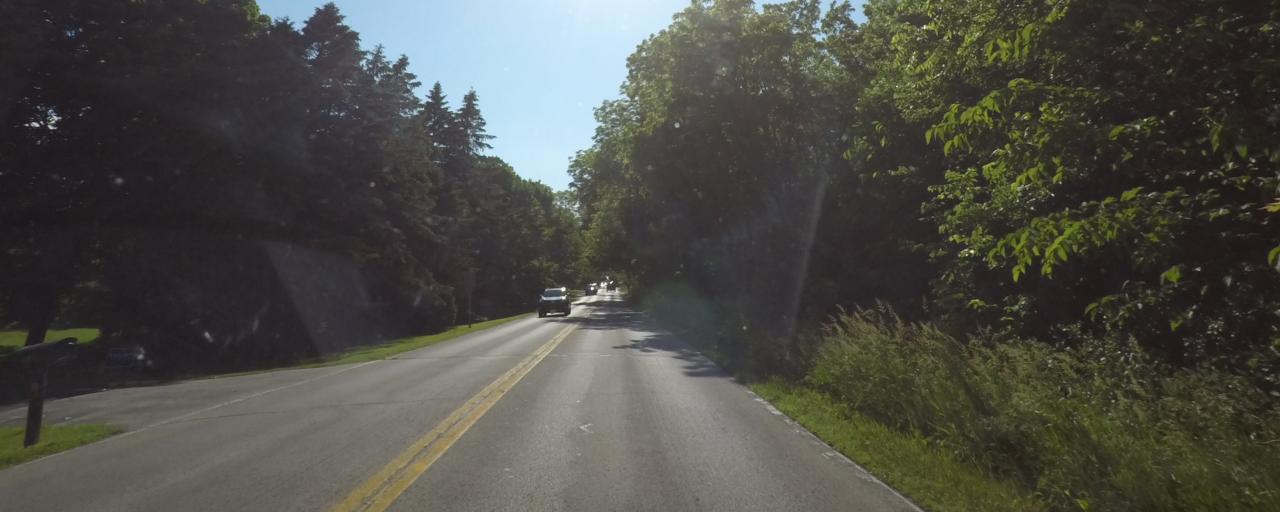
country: US
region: Wisconsin
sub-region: Milwaukee County
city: Greenfield
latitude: 42.9448
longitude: -88.0266
